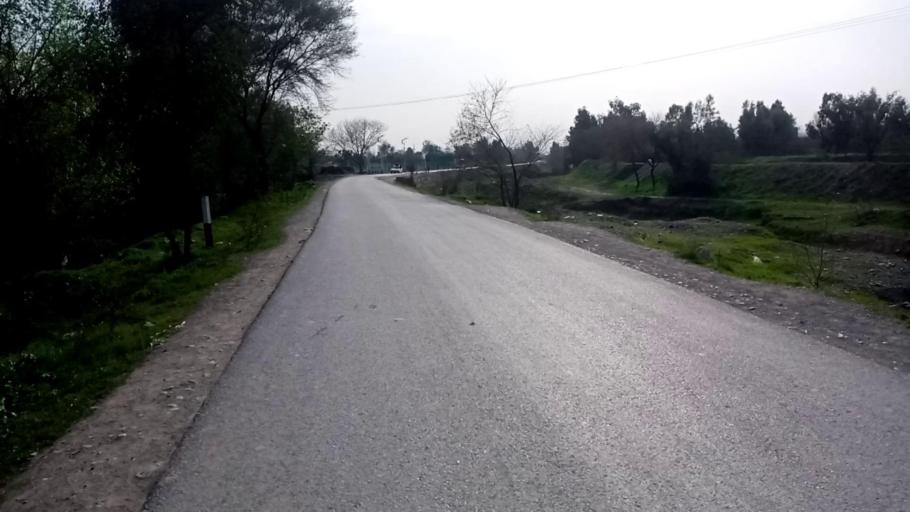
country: PK
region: Khyber Pakhtunkhwa
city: Peshawar
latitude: 34.0236
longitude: 71.4485
